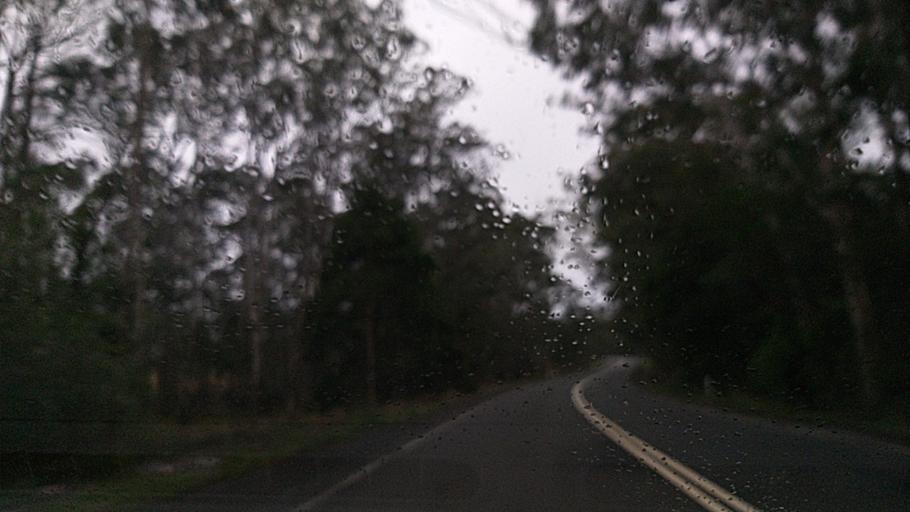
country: AU
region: New South Wales
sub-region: Wollondilly
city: Douglas Park
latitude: -34.2650
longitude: 150.7171
